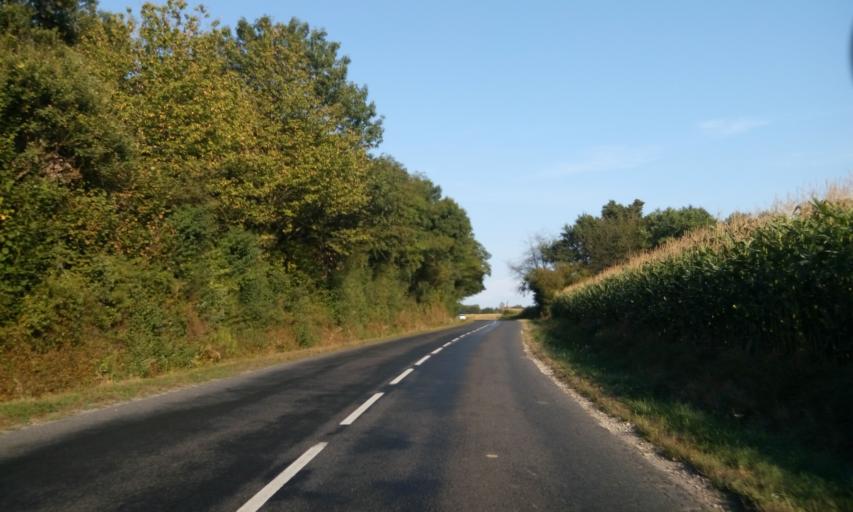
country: FR
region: Rhone-Alpes
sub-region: Departement de l'Ain
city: Amberieux-en-Dombes
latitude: 46.0009
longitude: 4.8802
